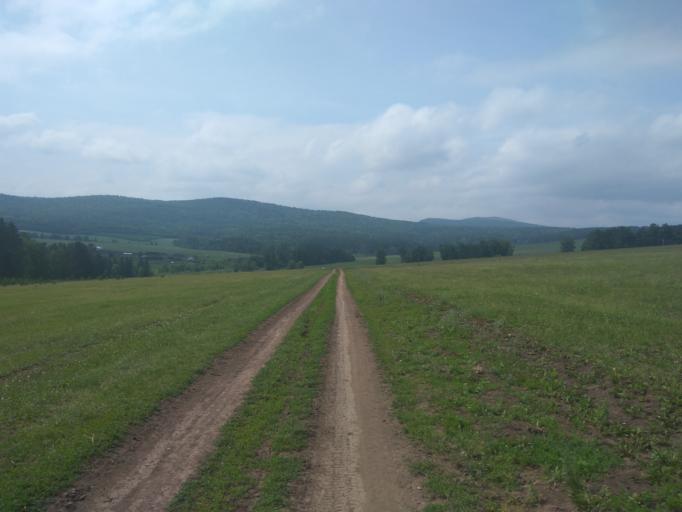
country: RU
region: Krasnoyarskiy
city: Zykovo
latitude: 55.8452
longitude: 93.2061
